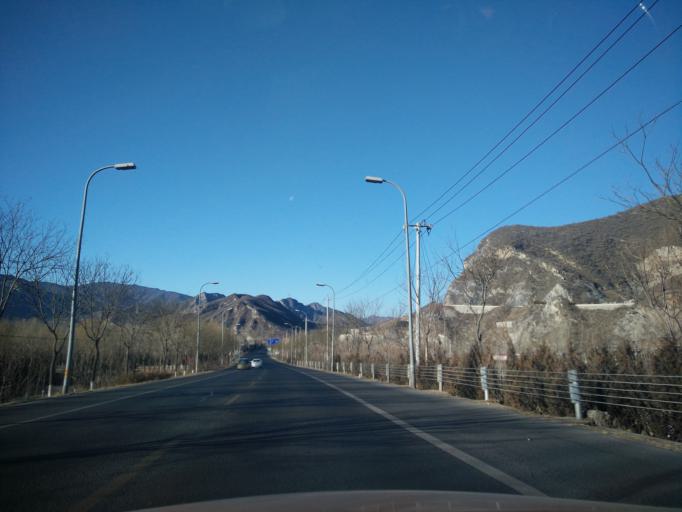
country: CN
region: Beijing
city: Miaofengshan
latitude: 39.9898
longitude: 116.0680
